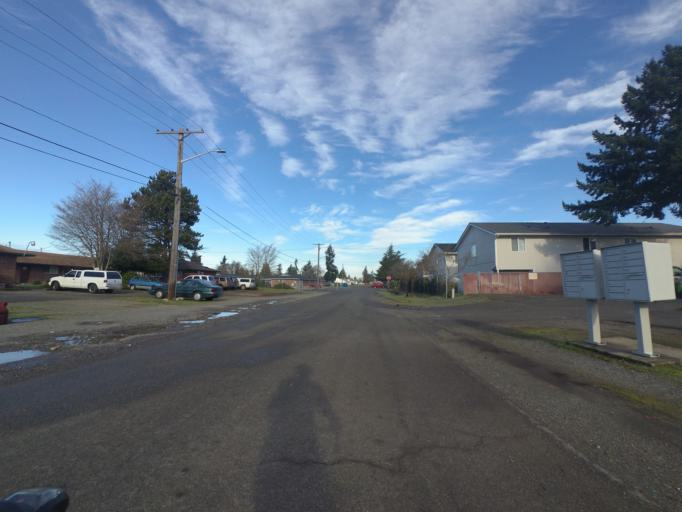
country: US
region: Washington
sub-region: Pierce County
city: Lakewood
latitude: 47.1579
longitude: -122.5009
